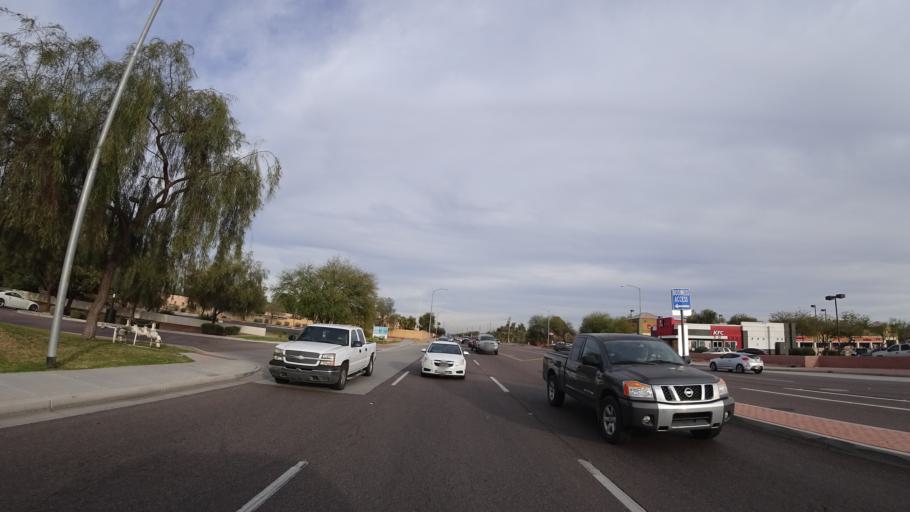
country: US
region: Arizona
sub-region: Maricopa County
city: Peoria
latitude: 33.5664
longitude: -112.2538
